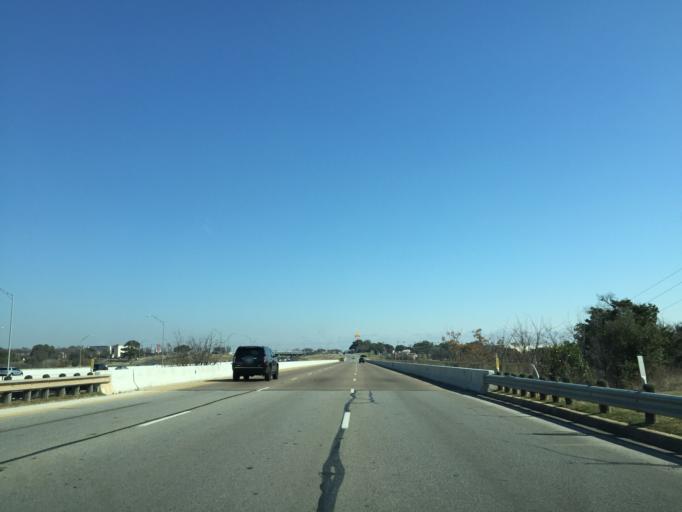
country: US
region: Texas
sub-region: Williamson County
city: Georgetown
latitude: 30.6445
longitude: -97.6841
